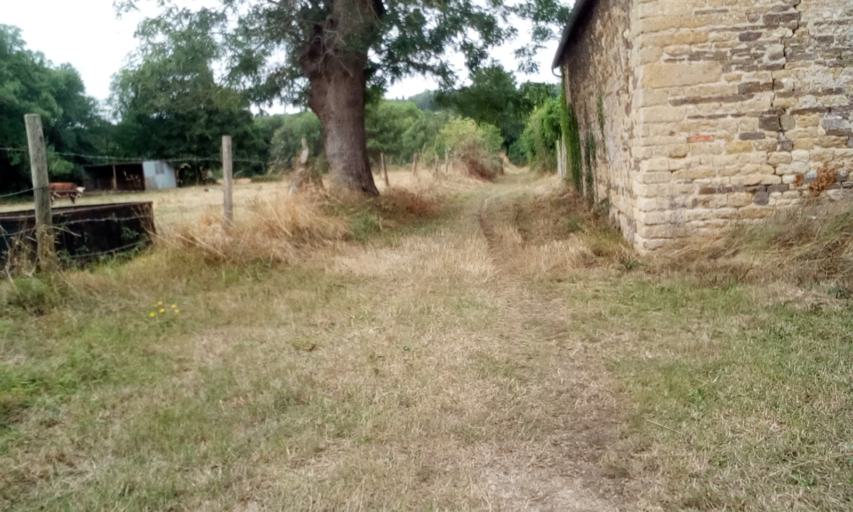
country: FR
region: Lower Normandy
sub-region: Departement du Calvados
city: Mouen
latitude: 49.1331
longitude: -0.4890
